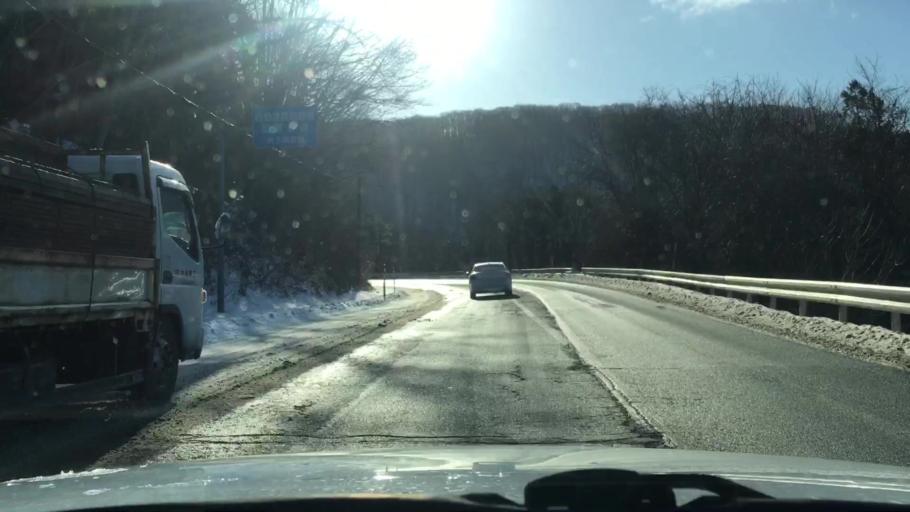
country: JP
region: Iwate
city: Morioka-shi
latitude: 39.6572
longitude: 141.3403
